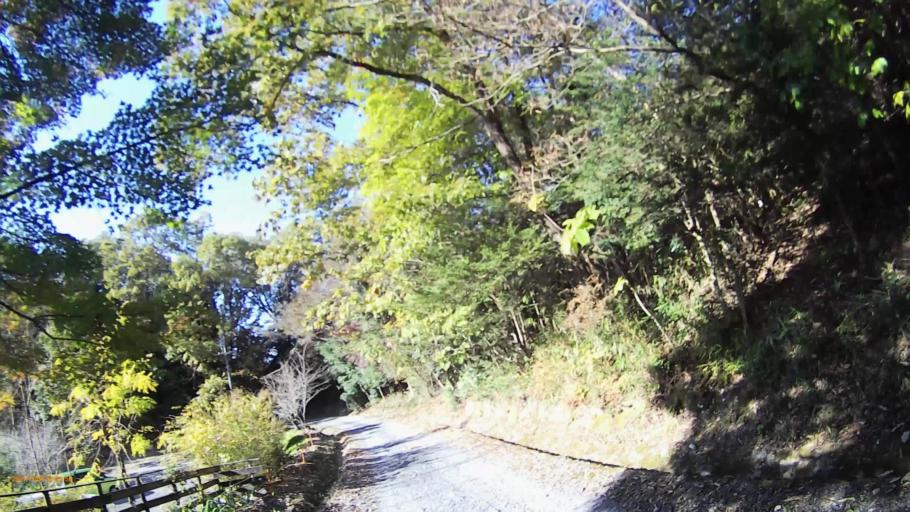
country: JP
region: Gifu
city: Mitake
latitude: 35.4290
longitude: 137.1815
